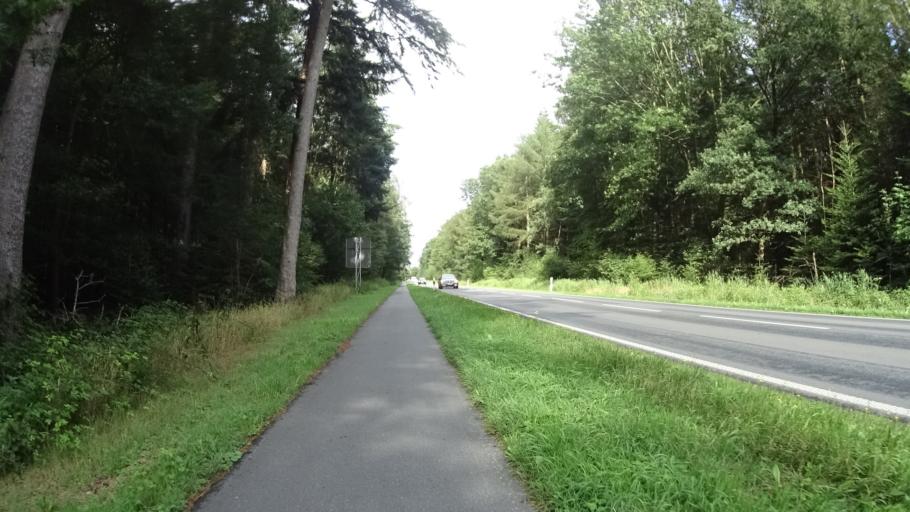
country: DE
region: Lower Saxony
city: Bockhorn
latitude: 53.3863
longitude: 8.0748
